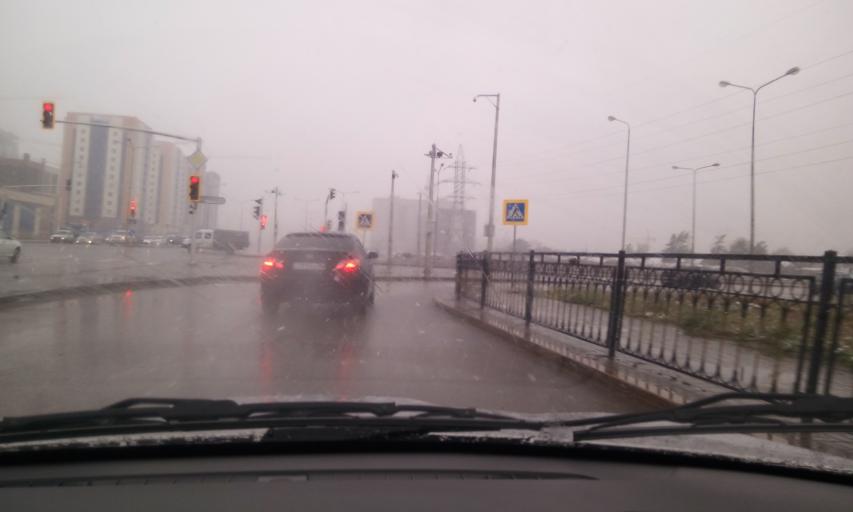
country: KZ
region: Astana Qalasy
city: Astana
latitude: 51.1480
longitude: 71.3691
